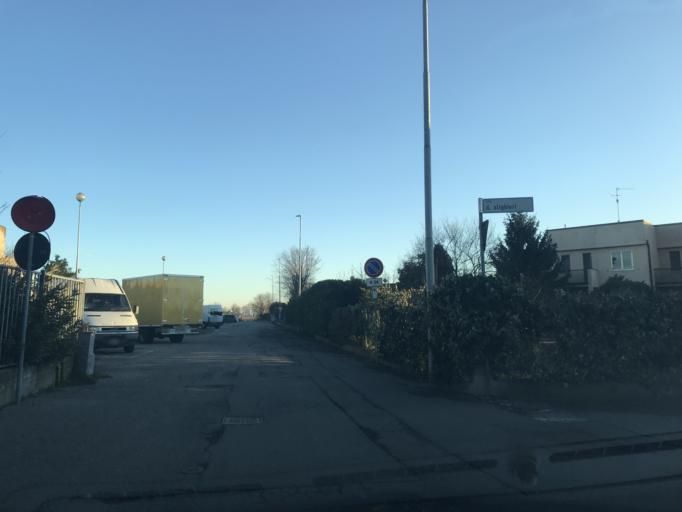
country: IT
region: Lombardy
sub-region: Provincia di Lodi
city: Massalengo-Motta Vigana
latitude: 45.2537
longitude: 9.5032
